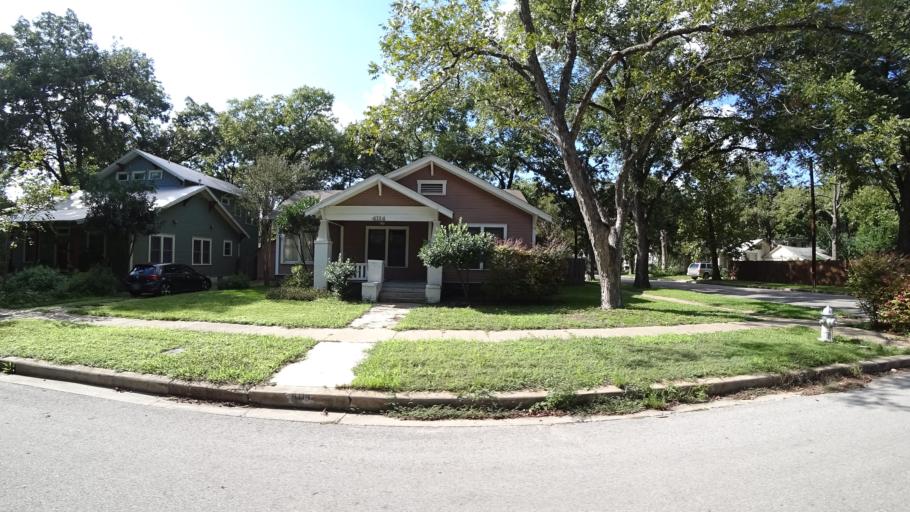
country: US
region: Texas
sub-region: Travis County
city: Austin
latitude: 30.3060
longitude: -97.7325
